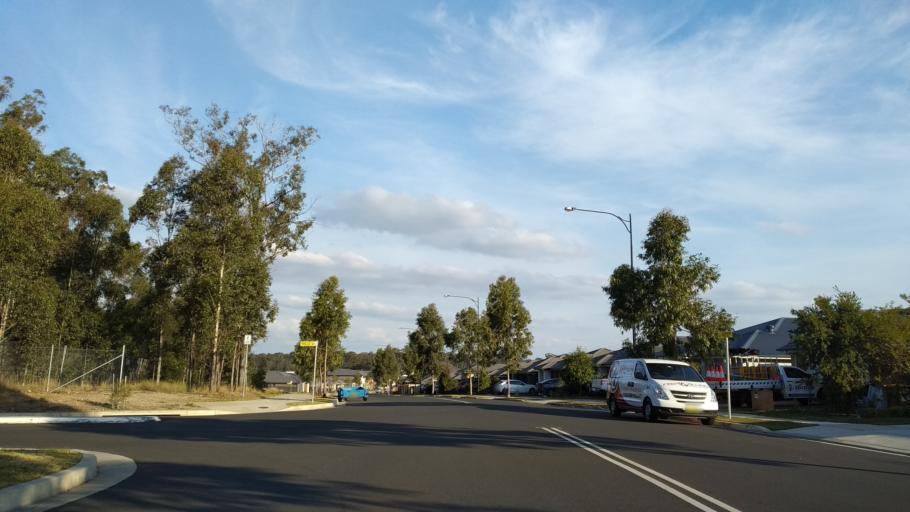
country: AU
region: New South Wales
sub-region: Penrith Municipality
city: Werrington Downs
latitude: -33.7232
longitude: 150.7356
